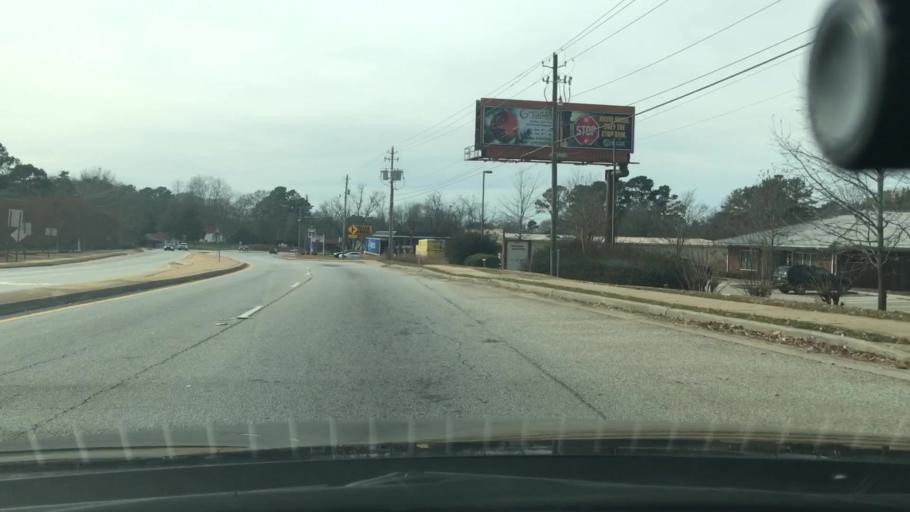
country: US
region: Georgia
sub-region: Spalding County
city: Experiment
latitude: 33.2742
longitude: -84.2963
